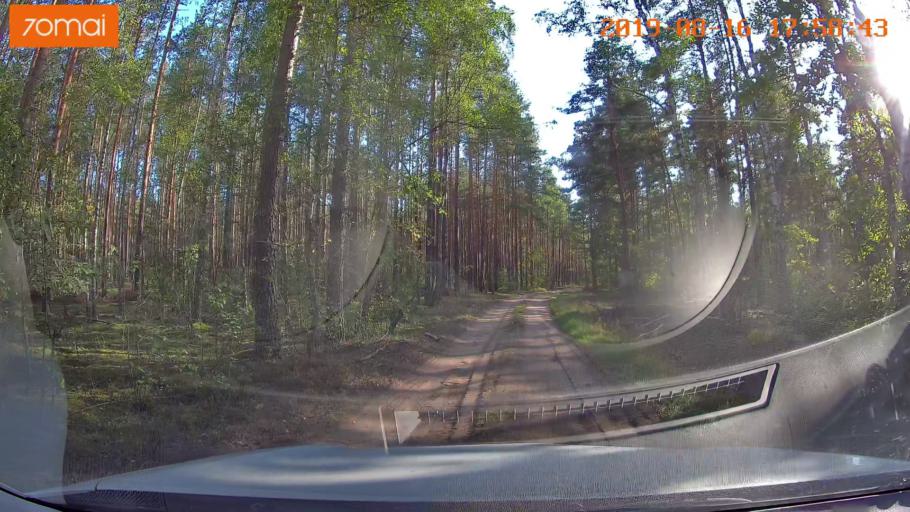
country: BY
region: Mogilev
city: Asipovichy
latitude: 53.2232
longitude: 28.6586
